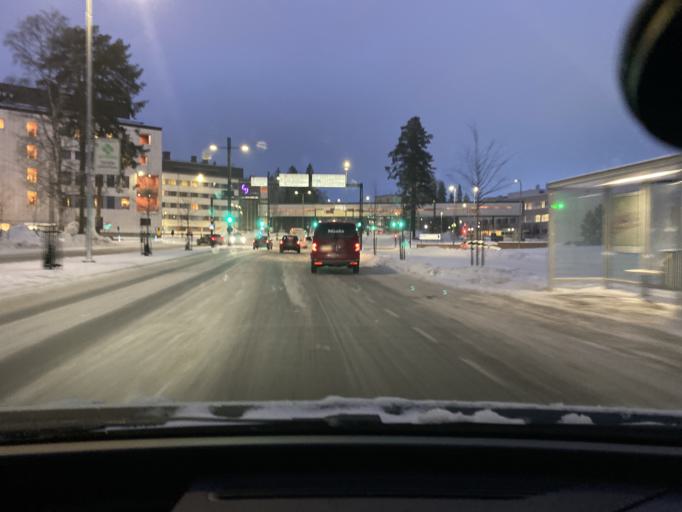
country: FI
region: Pirkanmaa
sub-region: Tampere
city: Tampere
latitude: 61.5034
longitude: 23.8115
